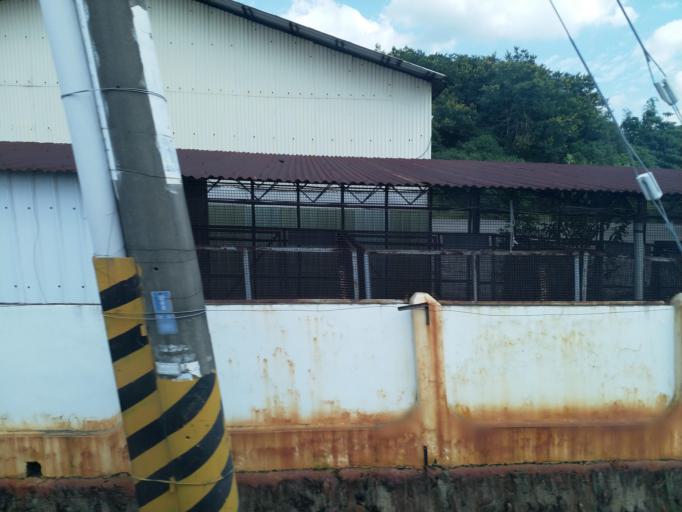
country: TW
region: Taiwan
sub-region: Pingtung
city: Pingtung
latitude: 22.8883
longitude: 120.5512
